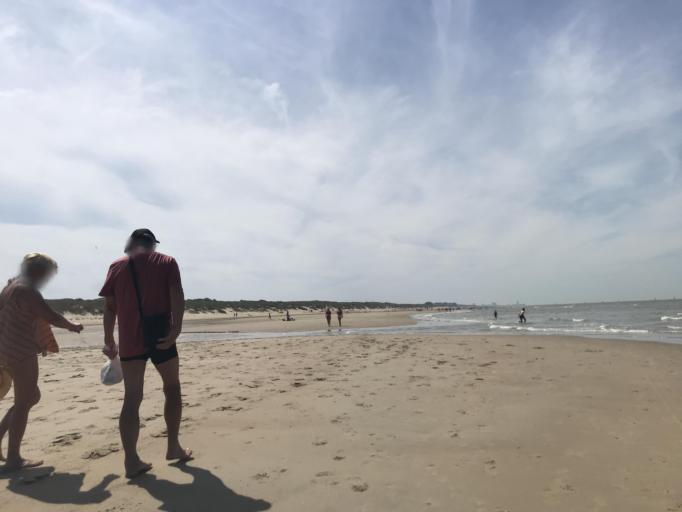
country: BE
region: Flanders
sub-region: Provincie West-Vlaanderen
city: Wenduine
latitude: 51.2927
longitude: 3.0575
